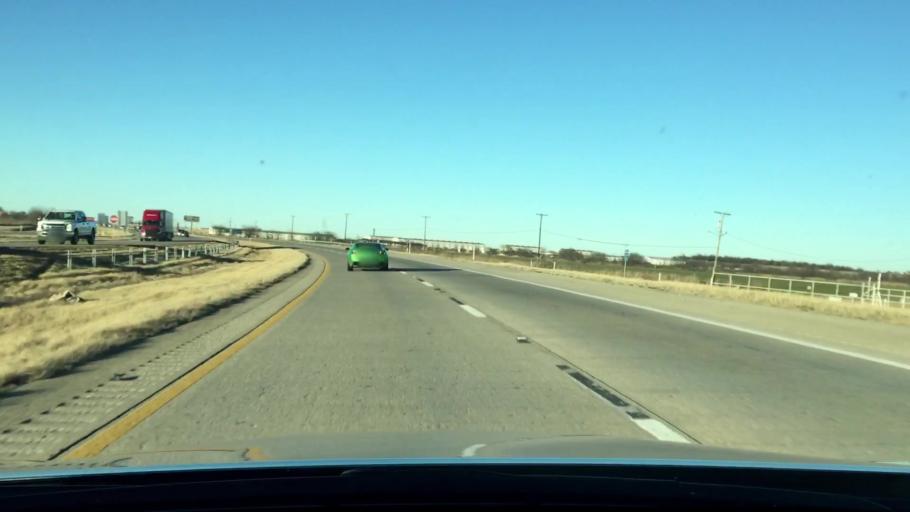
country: US
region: Texas
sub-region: Denton County
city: Sanger
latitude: 33.4394
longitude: -97.1646
